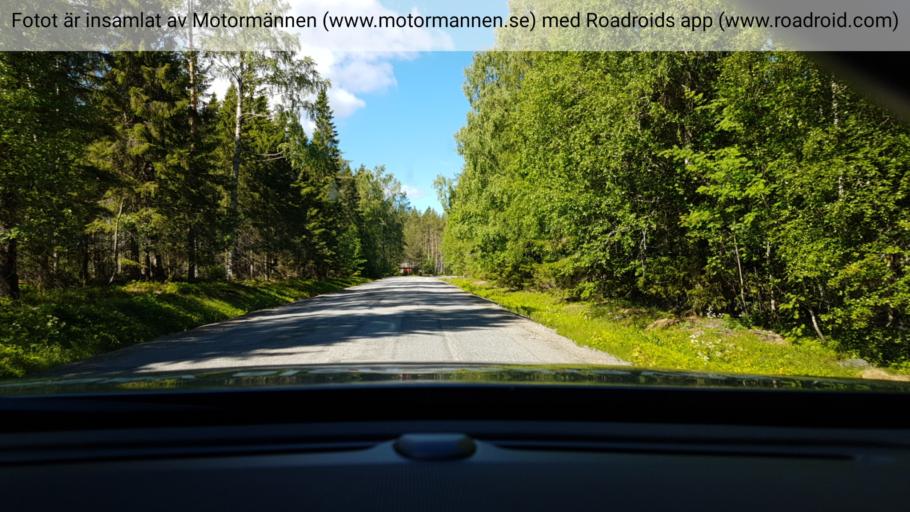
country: SE
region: Vaesterbotten
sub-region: Skelleftea Kommun
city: Burea
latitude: 64.4473
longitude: 21.4698
